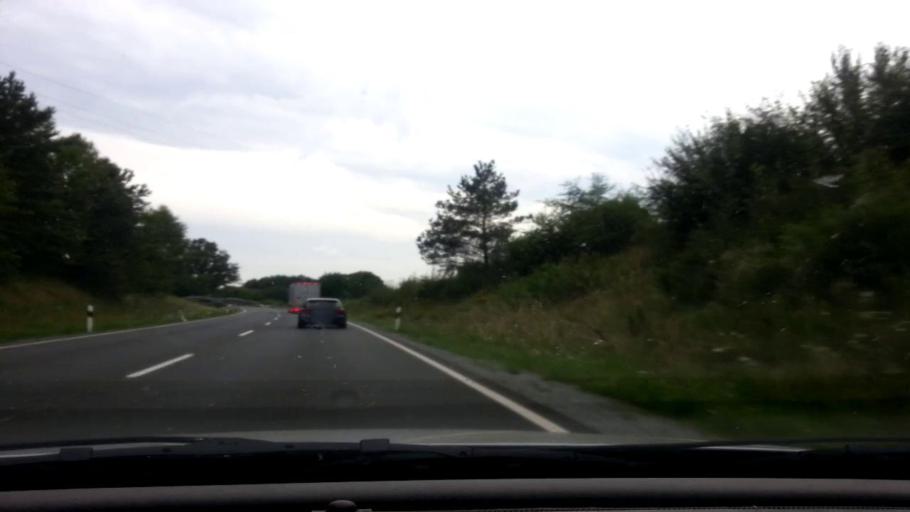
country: DE
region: Bavaria
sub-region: Upper Franconia
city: Seybothenreuth
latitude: 49.8961
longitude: 11.7115
